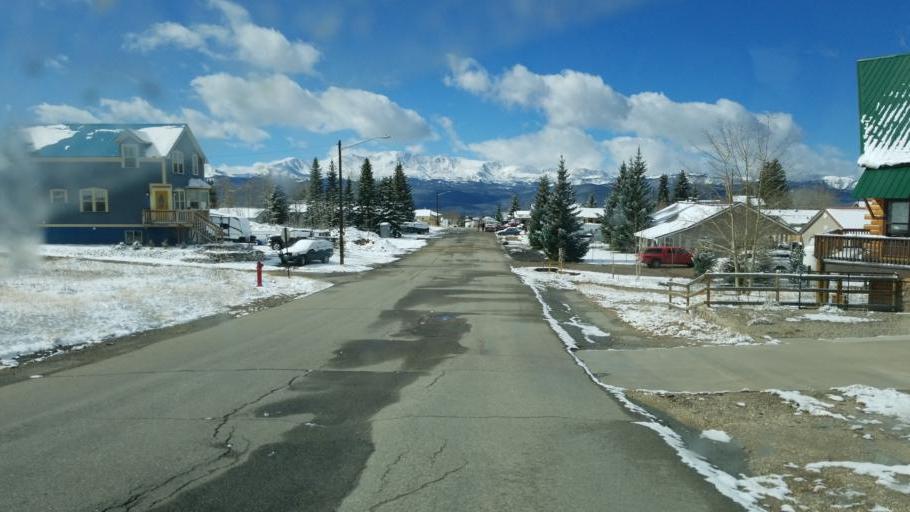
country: US
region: Colorado
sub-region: Lake County
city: Leadville
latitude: 39.2508
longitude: -106.2832
